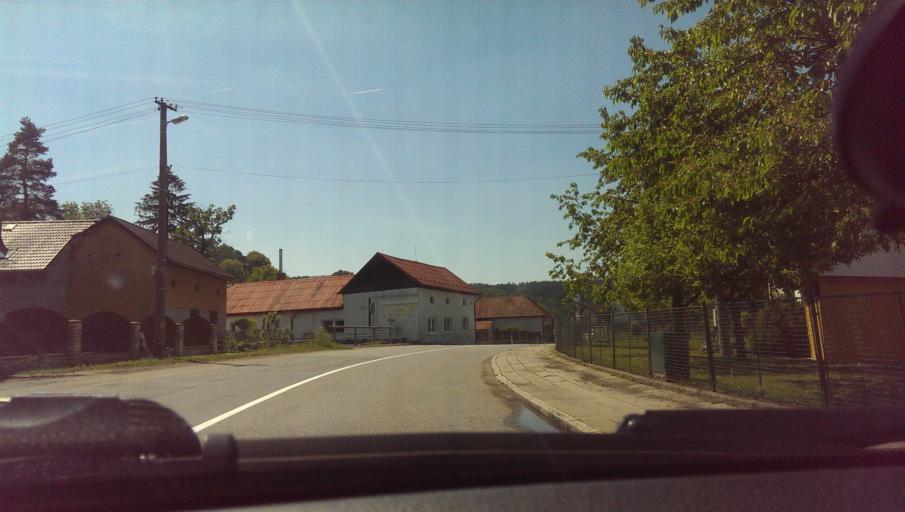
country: CZ
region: Zlin
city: Breznice
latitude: 49.1676
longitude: 17.6397
